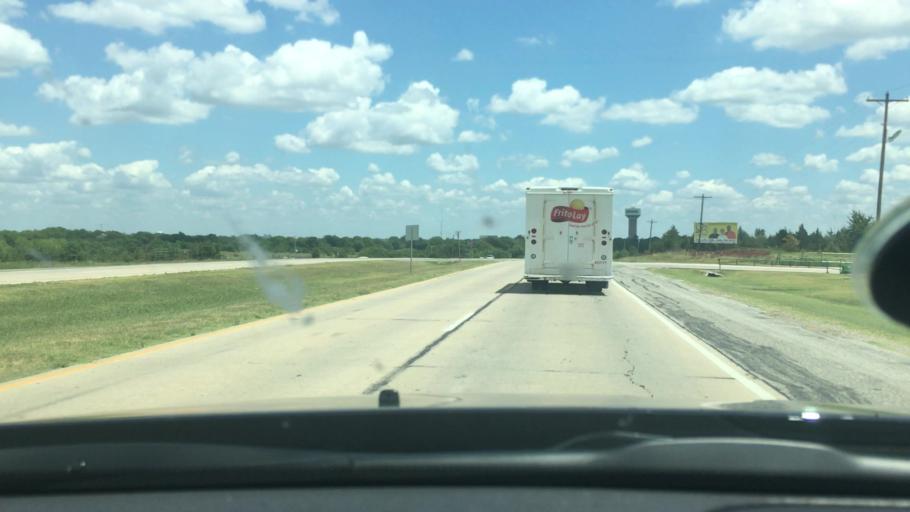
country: US
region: Oklahoma
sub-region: Carter County
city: Lone Grove
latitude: 34.1728
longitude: -97.2094
